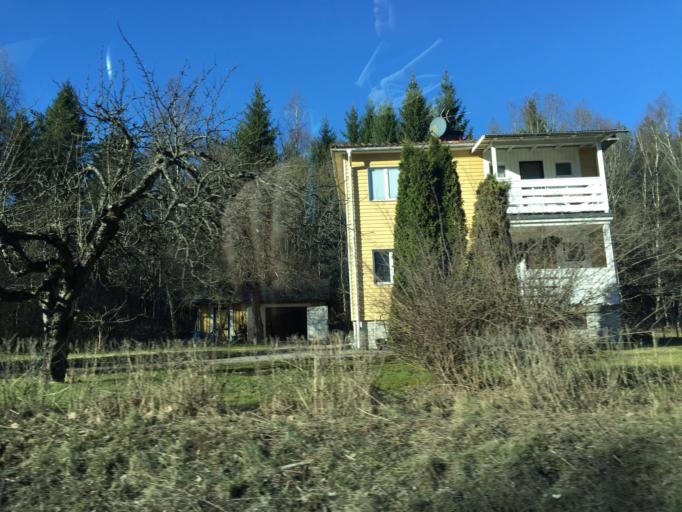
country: SE
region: OEstergoetland
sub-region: Finspangs Kommun
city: Finspang
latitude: 58.7096
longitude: 15.7379
